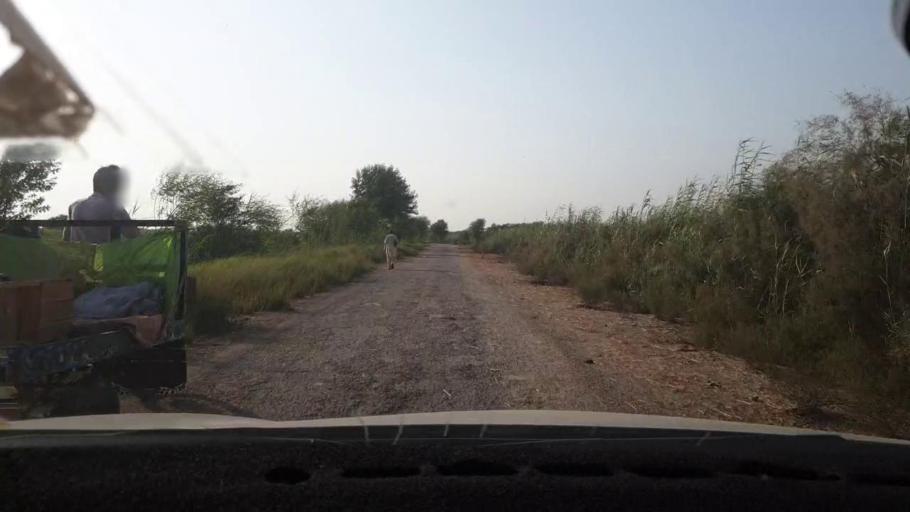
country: PK
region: Sindh
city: Berani
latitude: 25.8158
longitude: 68.8000
